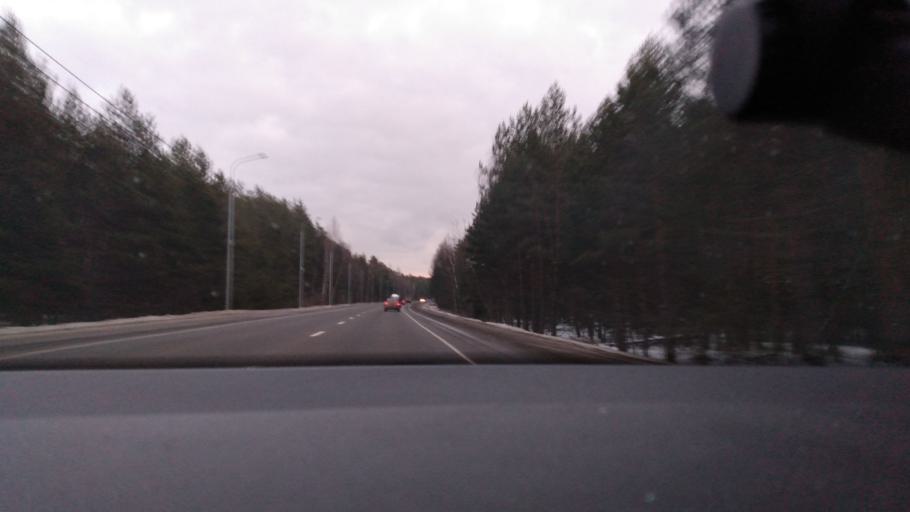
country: RU
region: Moskovskaya
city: Il'inskiy Pogost
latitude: 55.4756
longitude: 38.9506
